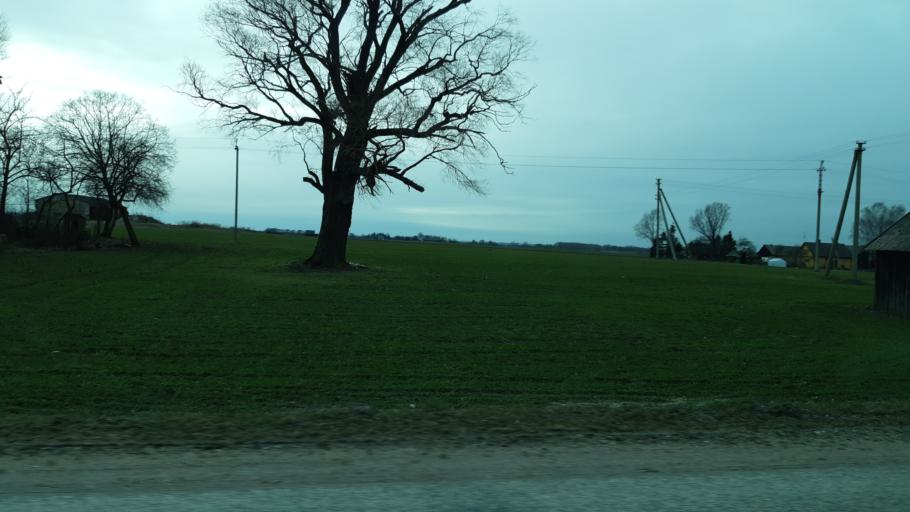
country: LT
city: Kybartai
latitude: 54.5697
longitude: 22.7242
